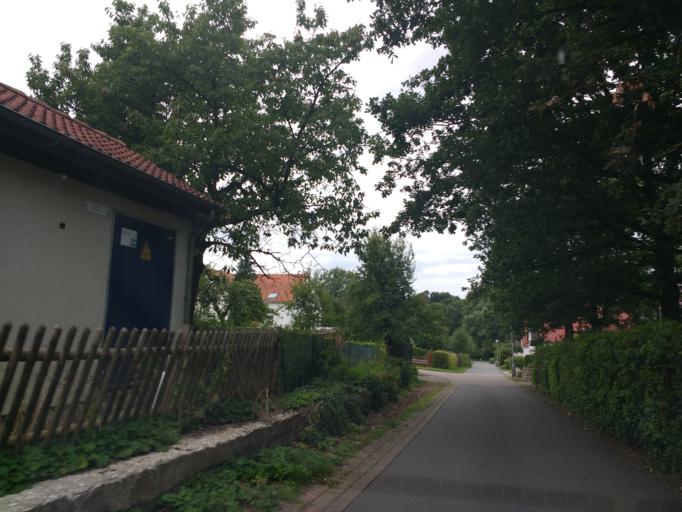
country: DE
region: North Rhine-Westphalia
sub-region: Regierungsbezirk Detmold
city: Bad Meinberg
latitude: 51.9148
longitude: 9.0300
